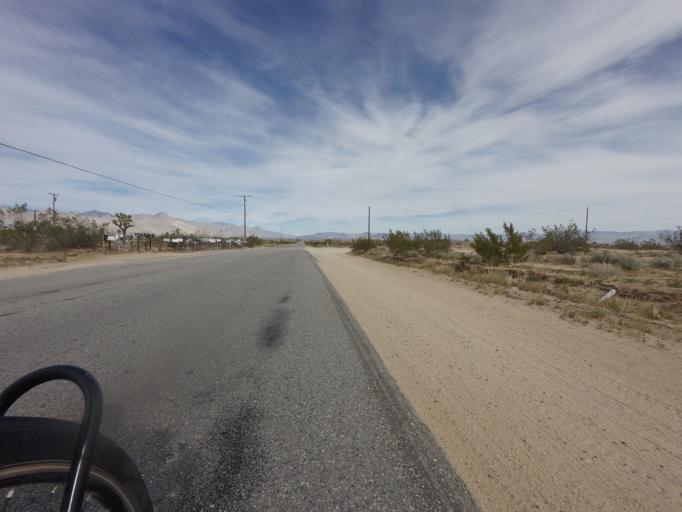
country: US
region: California
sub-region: Kern County
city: Inyokern
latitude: 35.6953
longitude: -117.8267
